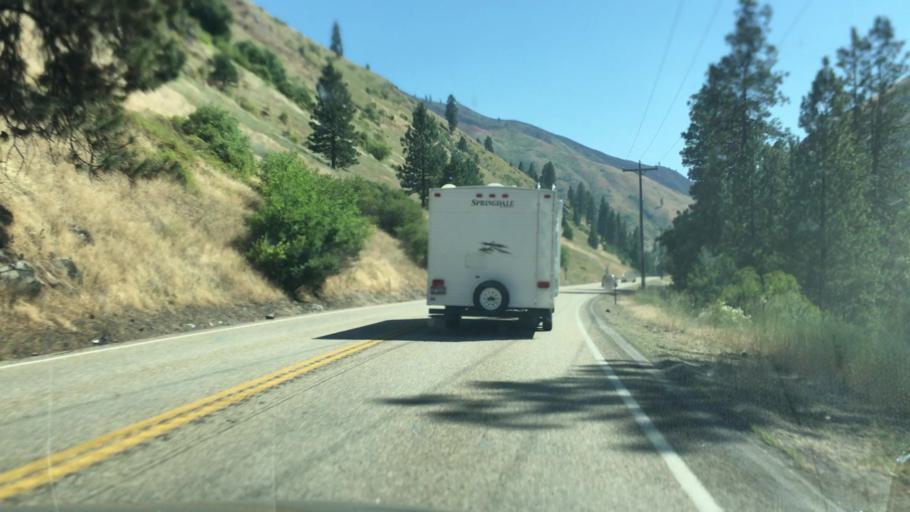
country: US
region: Idaho
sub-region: Boise County
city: Idaho City
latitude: 44.0434
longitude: -116.1307
